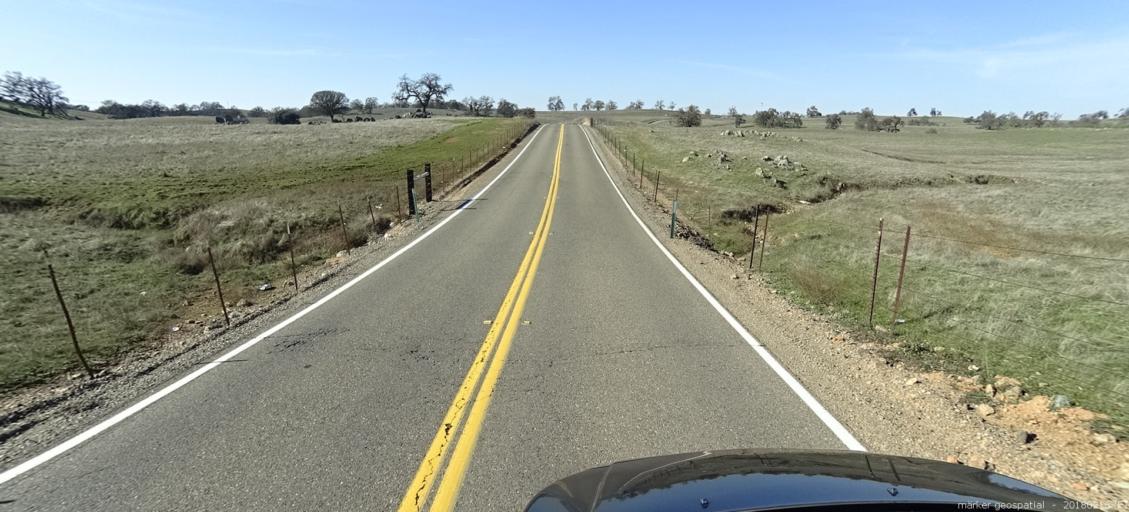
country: US
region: California
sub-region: Sacramento County
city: Rancho Murieta
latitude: 38.5607
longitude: -121.1241
